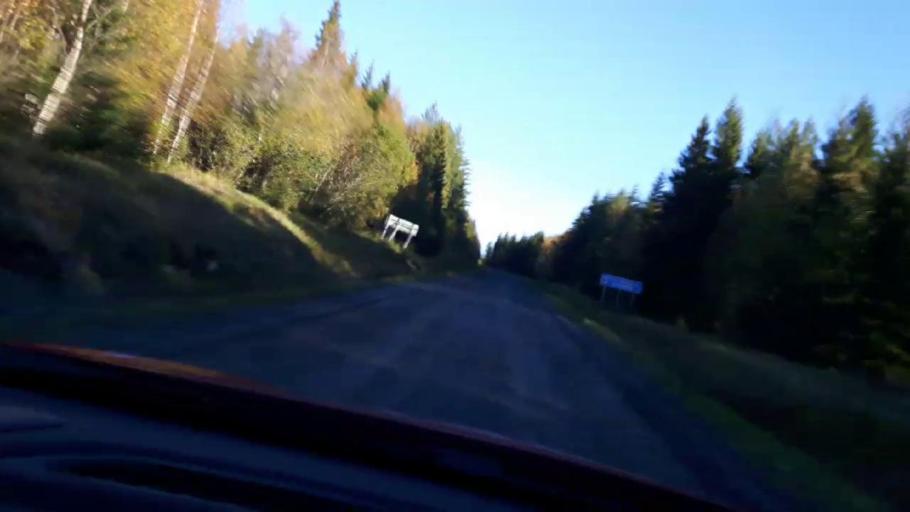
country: SE
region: Jaemtland
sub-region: OEstersunds Kommun
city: Lit
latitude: 63.5728
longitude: 14.8698
